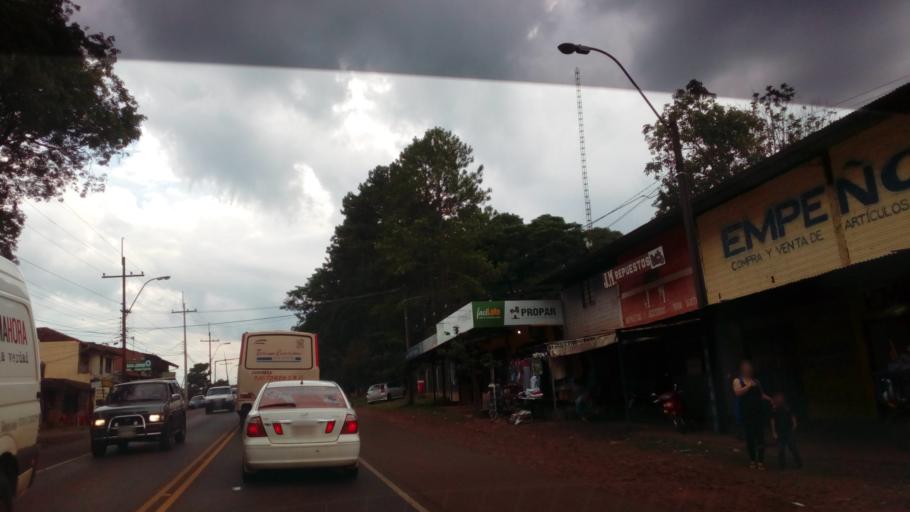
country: PY
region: Itapua
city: Obligado
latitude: -27.0813
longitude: -55.6472
